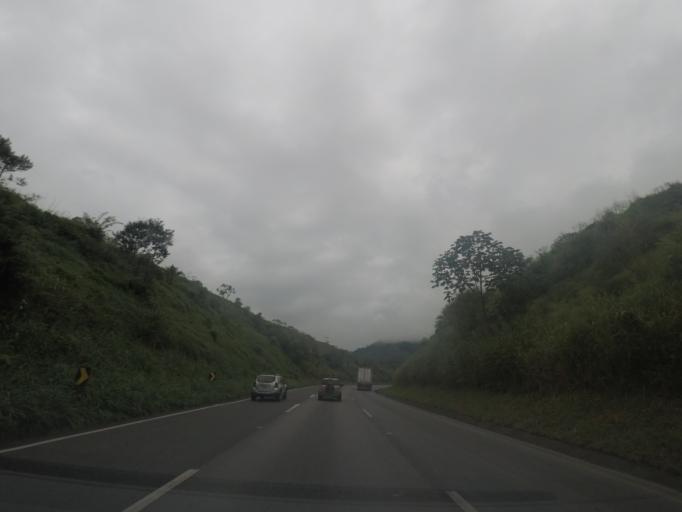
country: BR
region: Sao Paulo
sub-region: Cajati
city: Cajati
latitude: -24.8562
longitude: -48.2163
